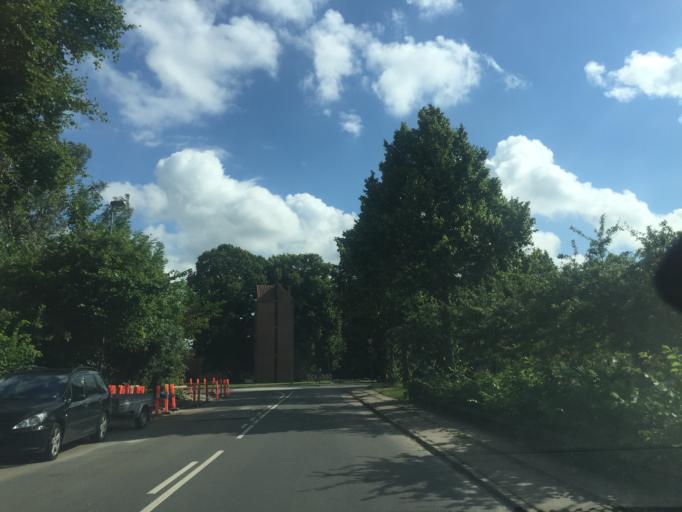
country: DK
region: South Denmark
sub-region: Odense Kommune
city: Odense
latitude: 55.3569
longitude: 10.3894
